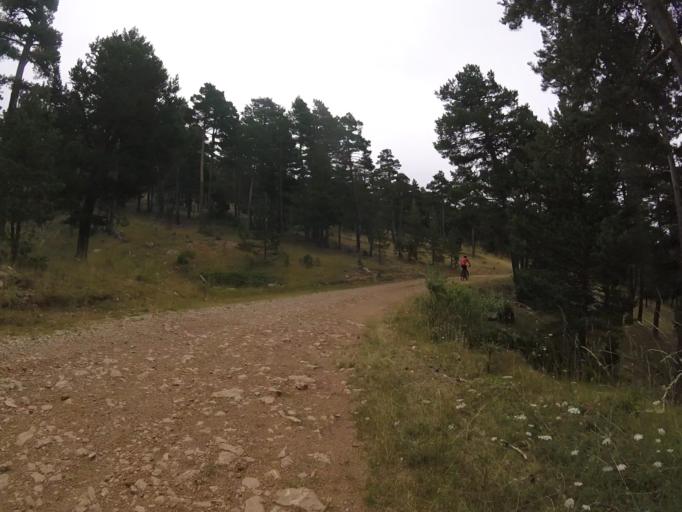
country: ES
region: Aragon
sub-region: Provincia de Teruel
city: Valdelinares
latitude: 40.3607
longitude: -0.6059
